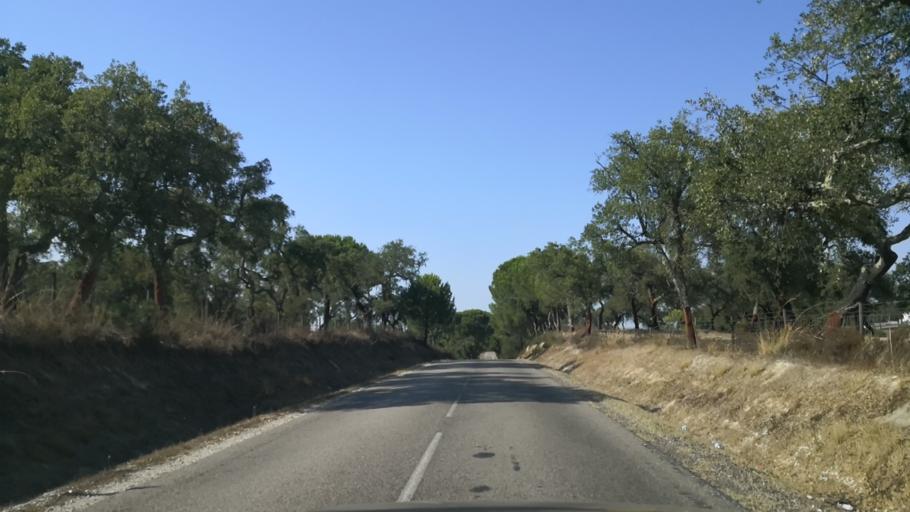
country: PT
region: Santarem
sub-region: Coruche
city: Coruche
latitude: 38.8515
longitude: -8.5448
